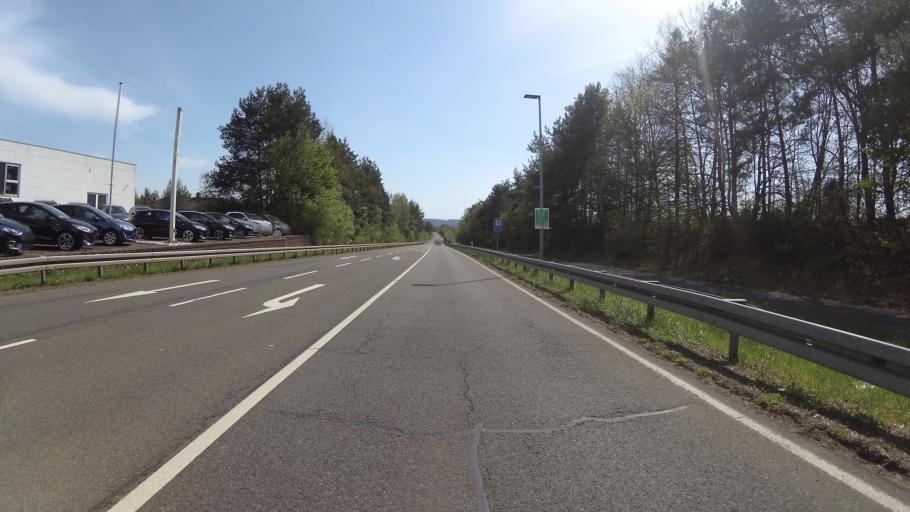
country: DE
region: Saarland
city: Homburg
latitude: 49.3451
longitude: 7.3423
